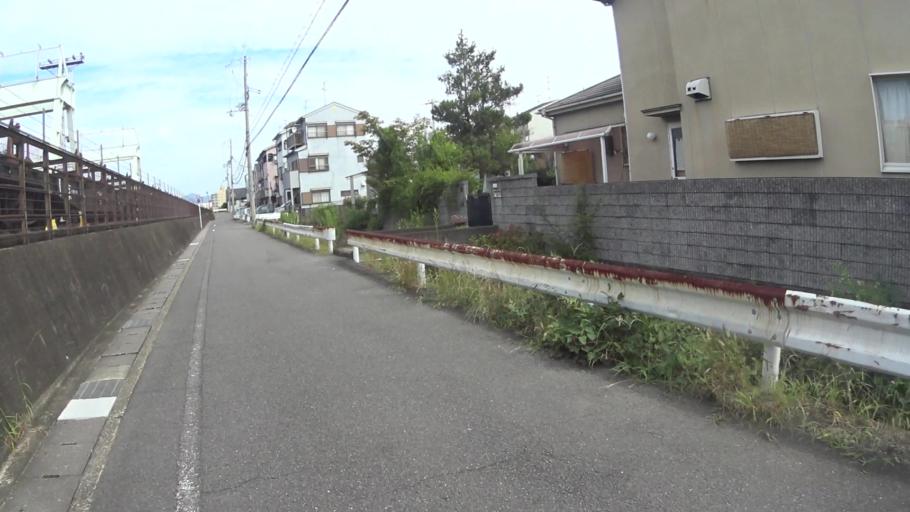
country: JP
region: Kyoto
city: Muko
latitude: 34.9463
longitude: 135.7106
